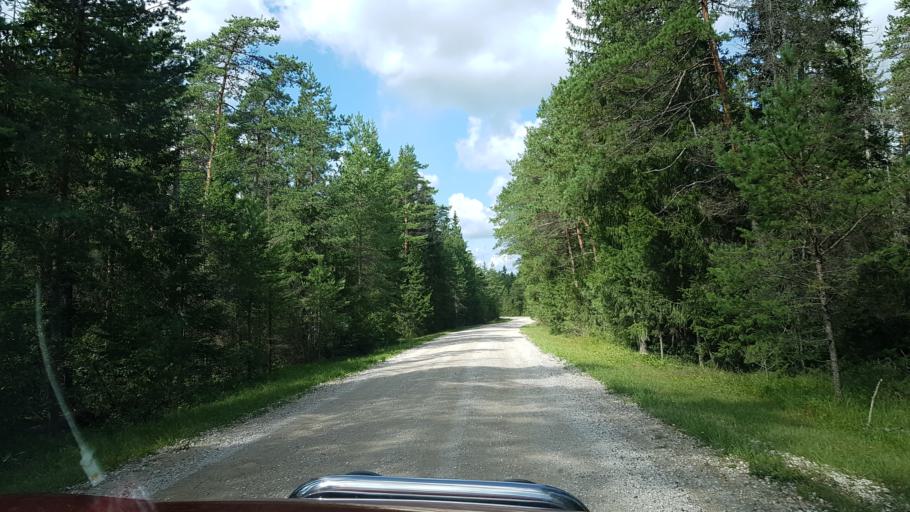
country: EE
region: Raplamaa
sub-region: Rapla vald
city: Rapla
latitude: 58.9569
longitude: 24.6565
